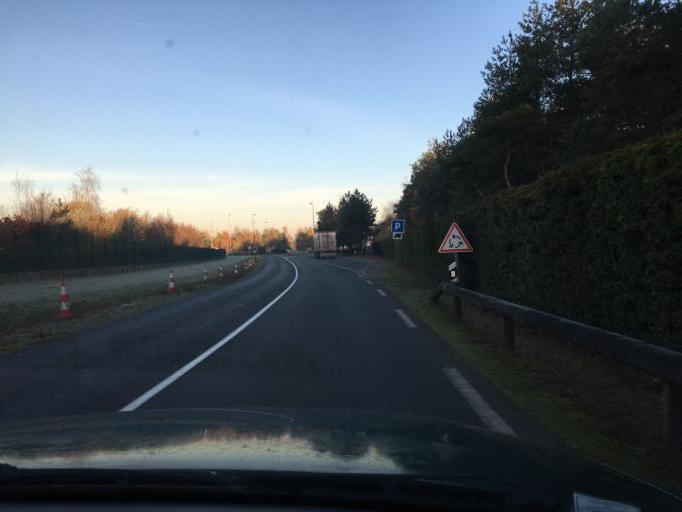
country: FR
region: Centre
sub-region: Departement du Loiret
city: Gidy
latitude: 47.9766
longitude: 1.8530
